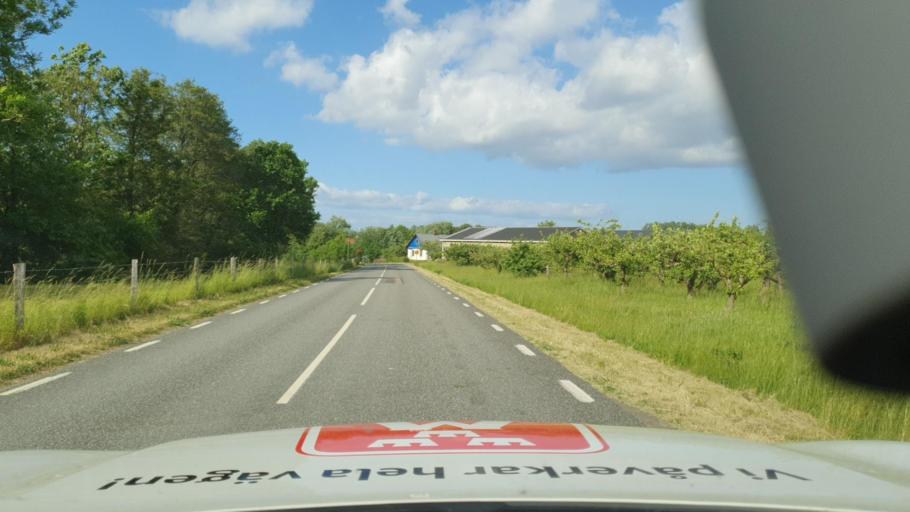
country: SE
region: Skane
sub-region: Simrishamns Kommun
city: Kivik
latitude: 55.6237
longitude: 14.2500
